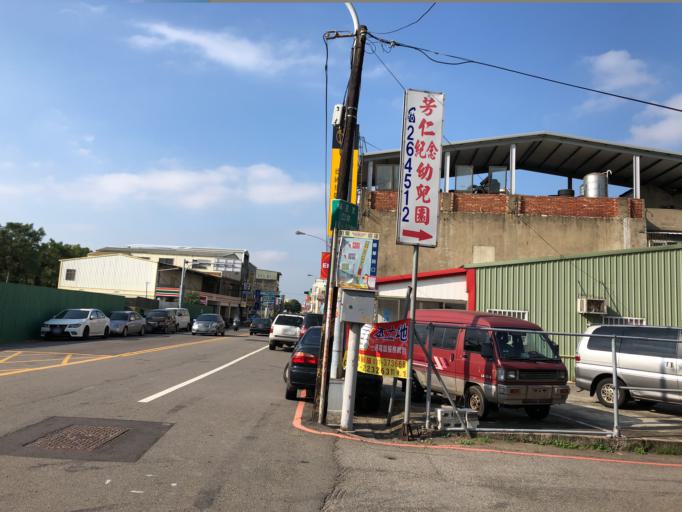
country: TW
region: Taiwan
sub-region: Miaoli
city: Miaoli
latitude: 24.5764
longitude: 120.8248
